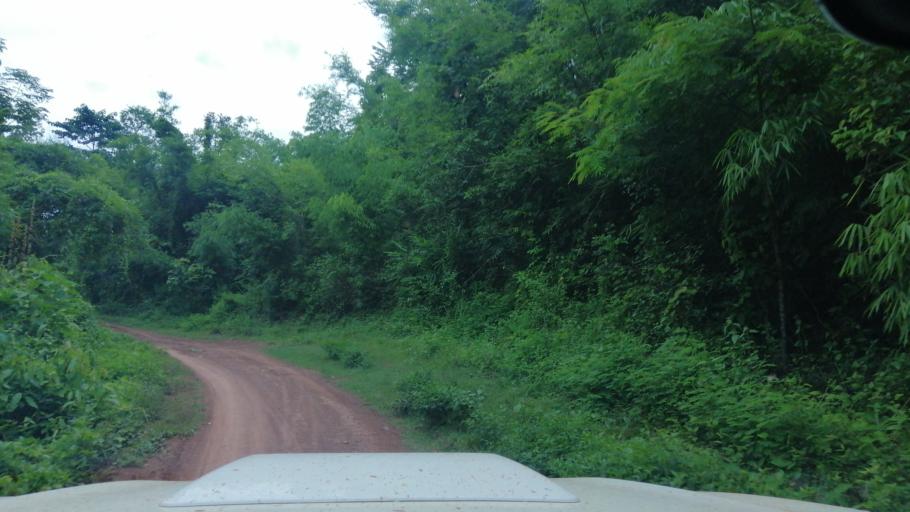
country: TH
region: Nan
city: Mae Charim
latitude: 18.7668
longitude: 101.3095
